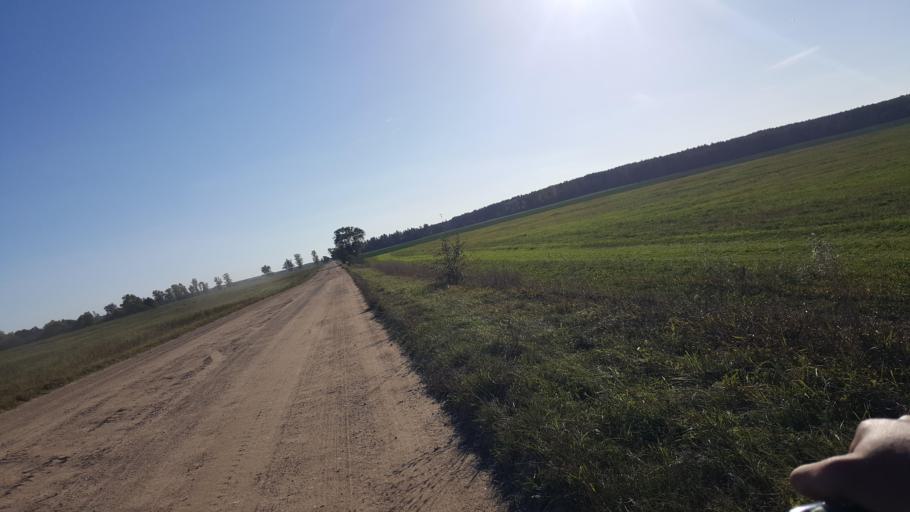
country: BY
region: Brest
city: Kamyanyets
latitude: 52.3828
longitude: 23.8826
